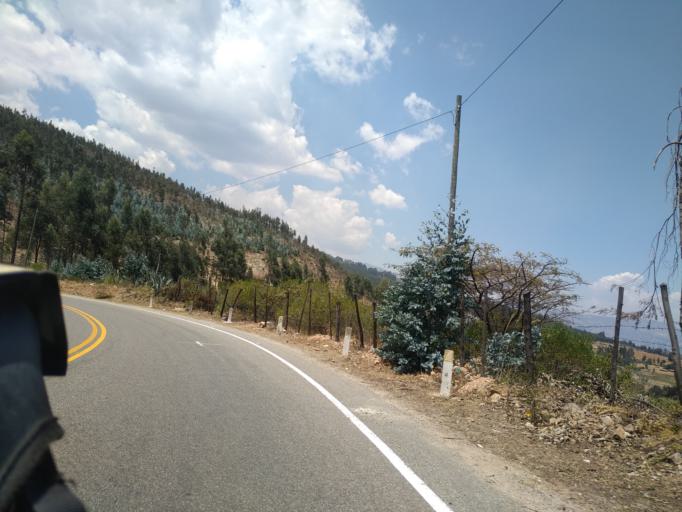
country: PE
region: Cajamarca
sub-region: San Marcos
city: San Marcos
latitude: -7.2861
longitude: -78.2121
